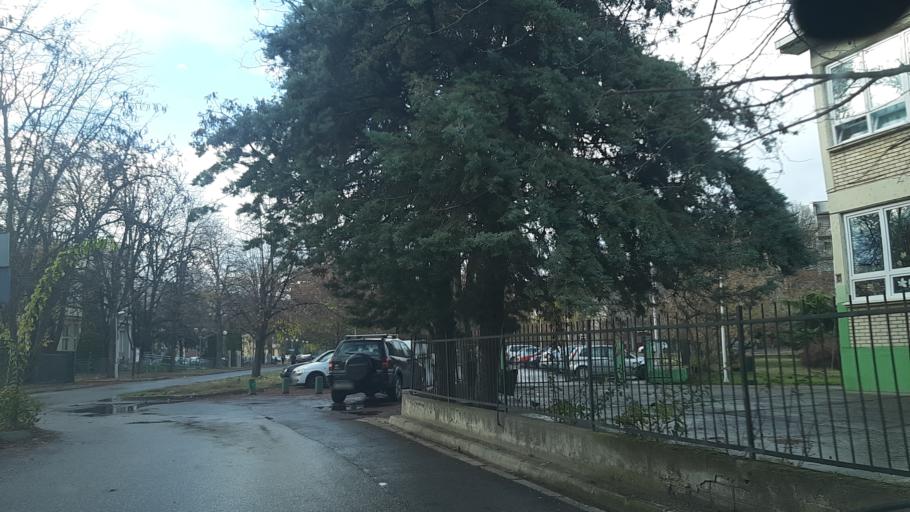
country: MK
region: Kisela Voda
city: Usje
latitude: 41.9839
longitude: 21.4600
